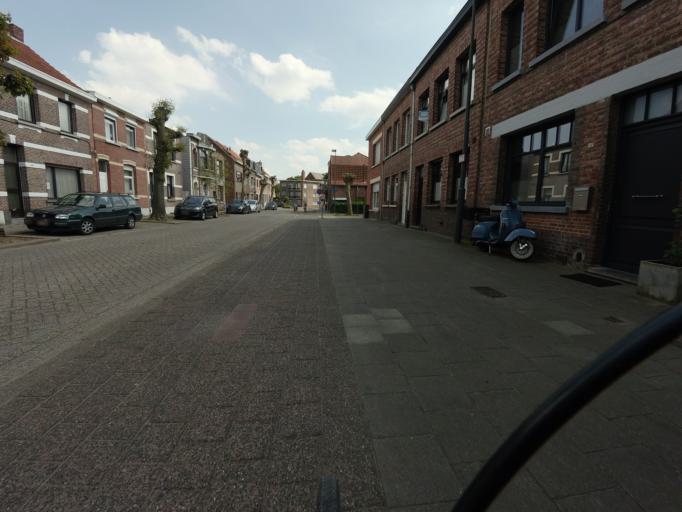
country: BE
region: Flanders
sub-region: Provincie Antwerpen
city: Hove
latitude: 51.1651
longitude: 4.4723
